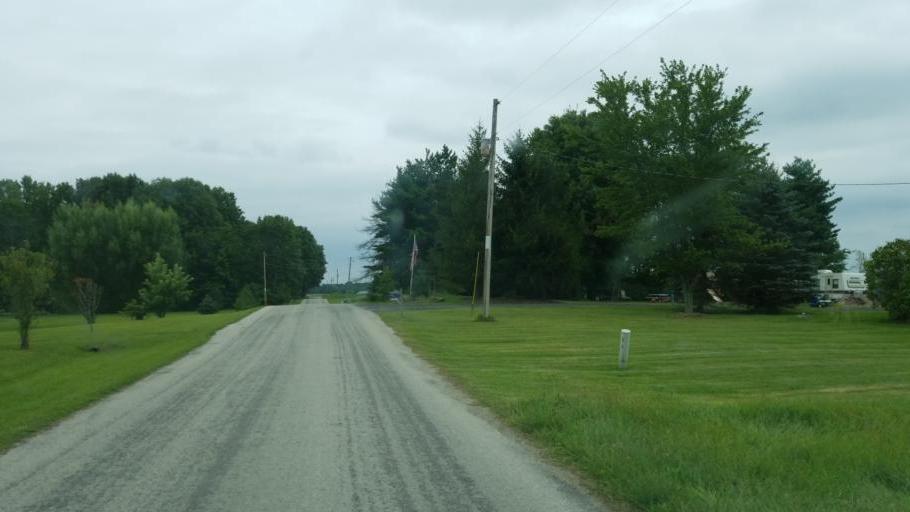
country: US
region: Ohio
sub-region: Morrow County
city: Mount Gilead
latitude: 40.5326
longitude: -82.8019
